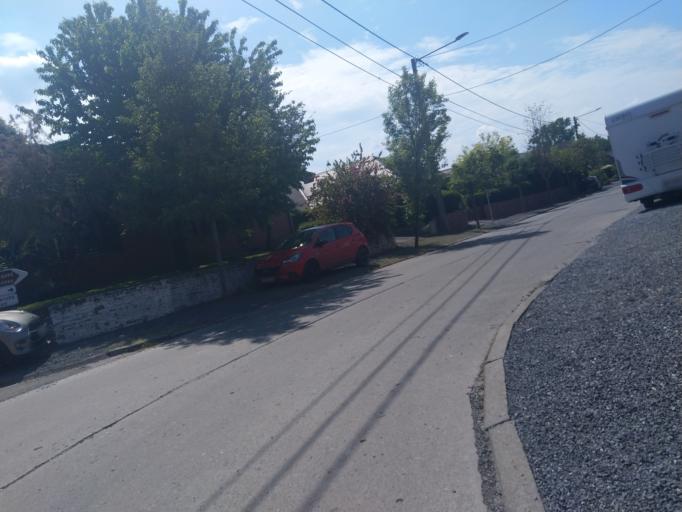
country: BE
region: Wallonia
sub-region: Province du Hainaut
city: Chasse Royale
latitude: 50.4252
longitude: 3.9894
